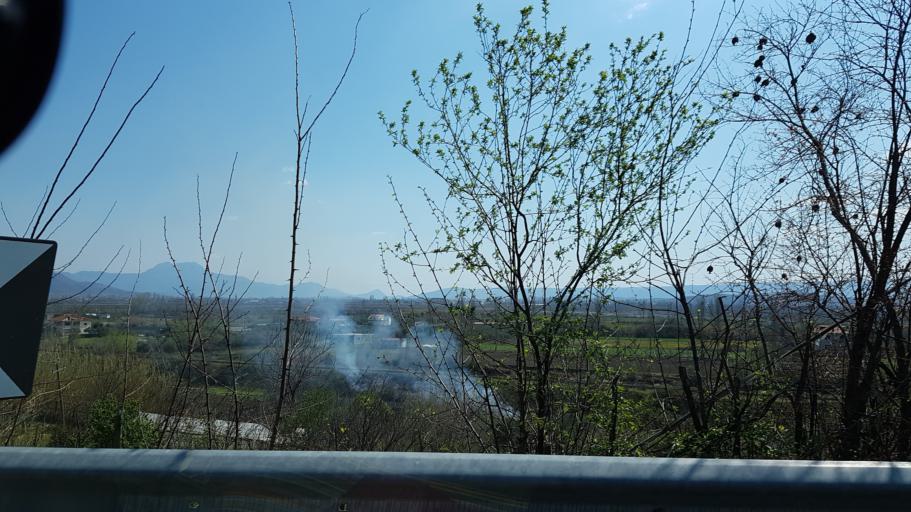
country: AL
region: Shkoder
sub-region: Rrethi i Shkodres
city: Vau i Dejes
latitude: 42.0118
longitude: 19.5887
